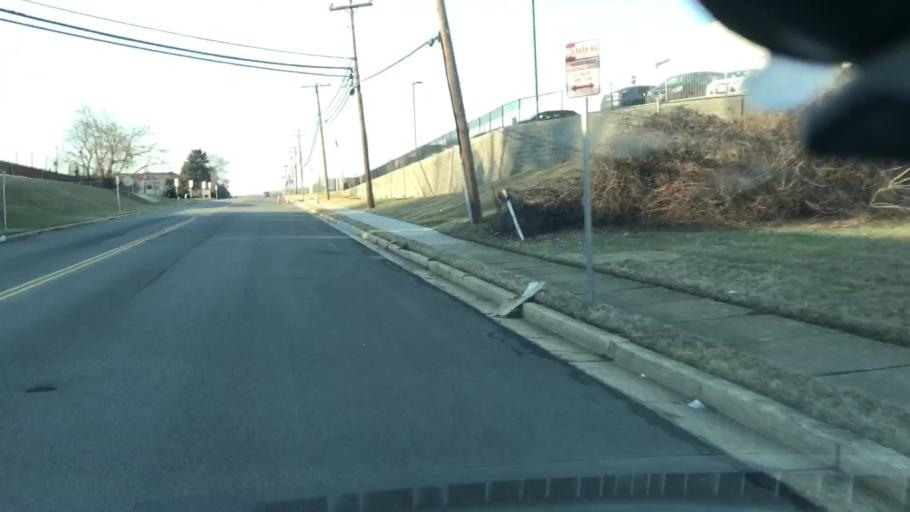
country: US
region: Virginia
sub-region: Fairfax County
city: Ravensworth
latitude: 38.8049
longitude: -77.2154
